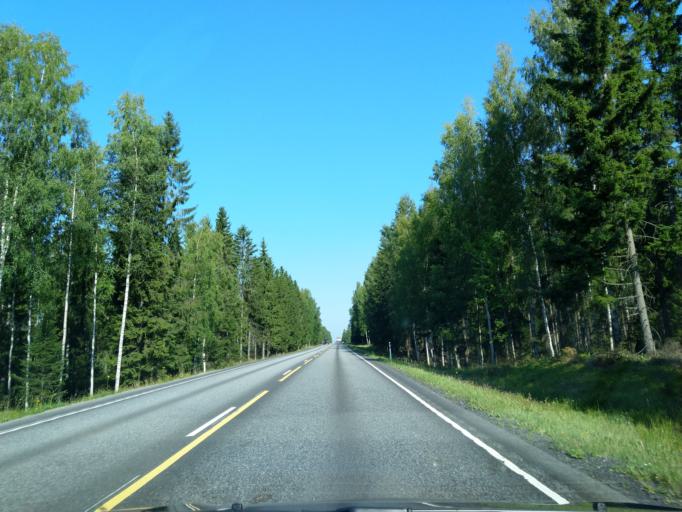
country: FI
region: Varsinais-Suomi
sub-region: Loimaa
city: Alastaro
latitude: 61.0728
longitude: 22.9177
